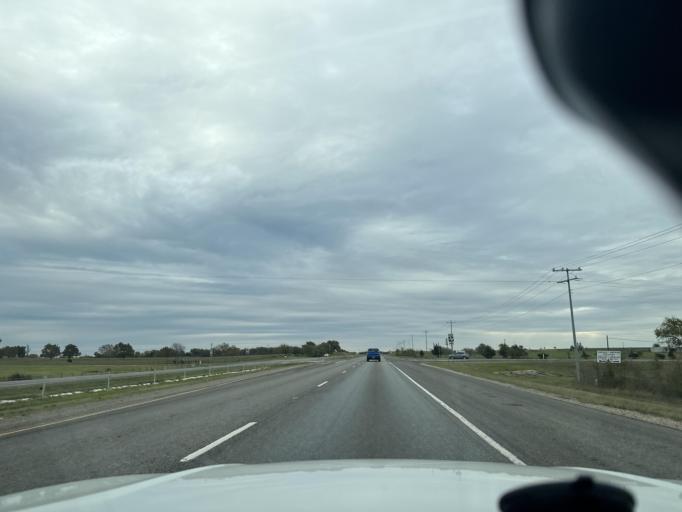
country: US
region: Texas
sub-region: Burleson County
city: Somerville
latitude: 30.1620
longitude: -96.6170
